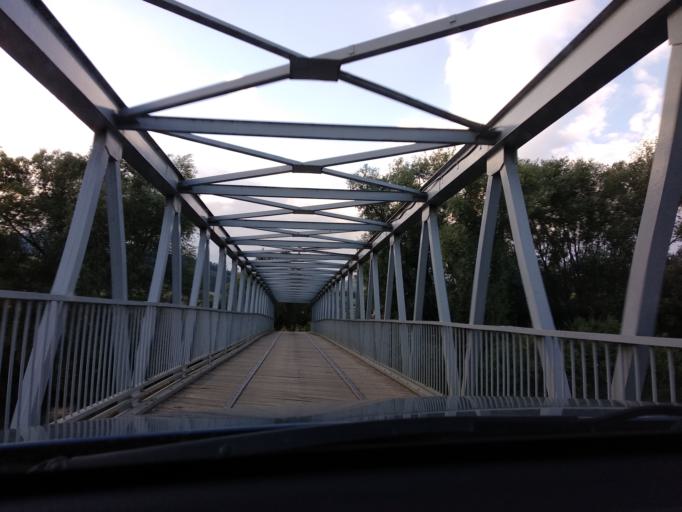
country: SK
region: Zilinsky
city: Ruzomberok
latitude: 49.0966
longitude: 19.4129
